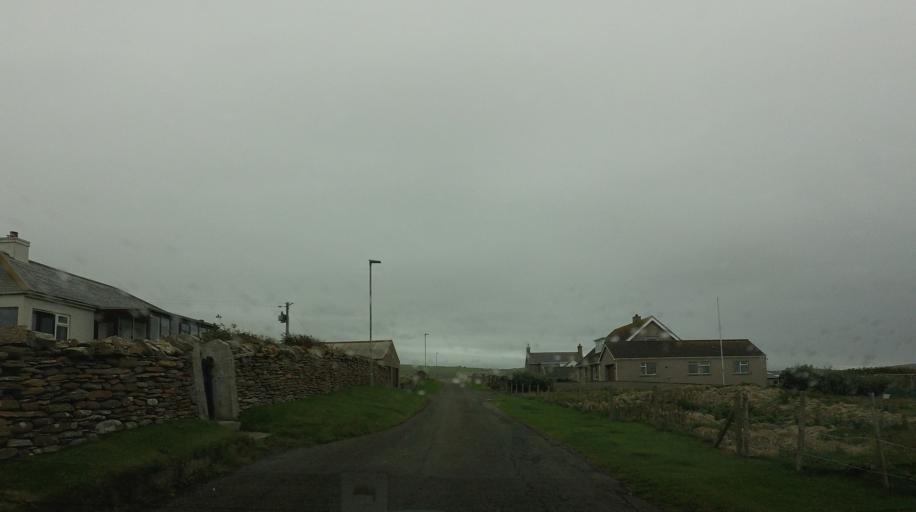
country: GB
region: Scotland
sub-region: Orkney Islands
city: Stromness
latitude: 59.1274
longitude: -3.3155
